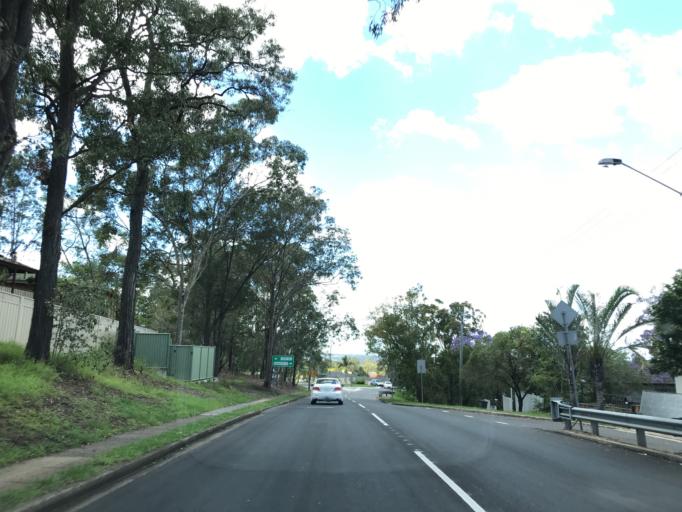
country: AU
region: Queensland
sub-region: Brisbane
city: Seventeen Mile Rocks
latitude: -27.5545
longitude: 152.9607
